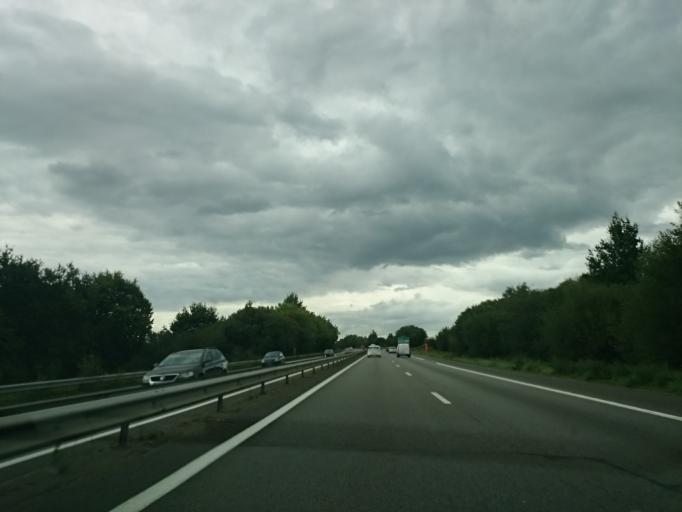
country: FR
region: Pays de la Loire
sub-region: Departement de la Loire-Atlantique
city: Orvault
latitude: 47.2834
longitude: -1.6047
